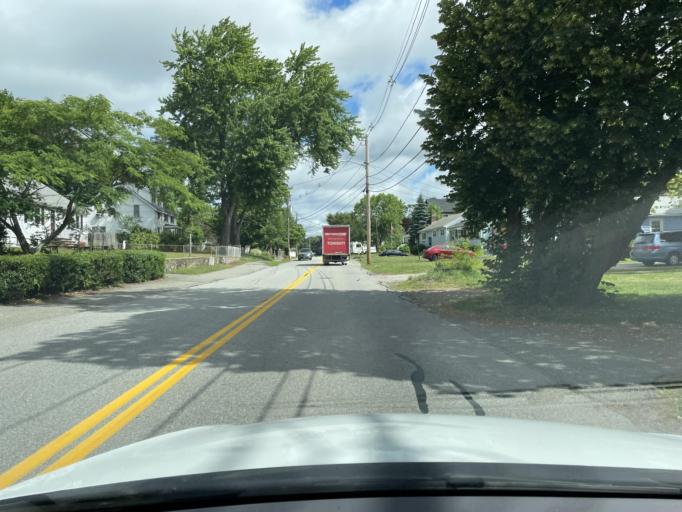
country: US
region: Massachusetts
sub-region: Middlesex County
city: Woburn
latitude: 42.4819
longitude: -71.1744
